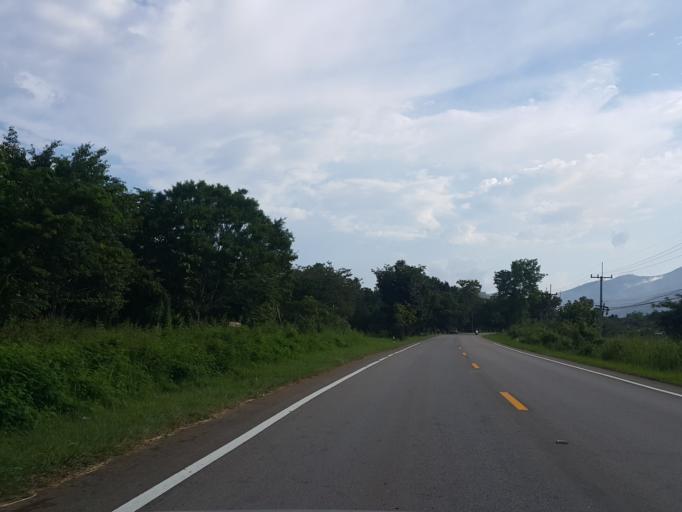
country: TH
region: Chiang Mai
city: Phrao
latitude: 19.2003
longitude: 99.1728
